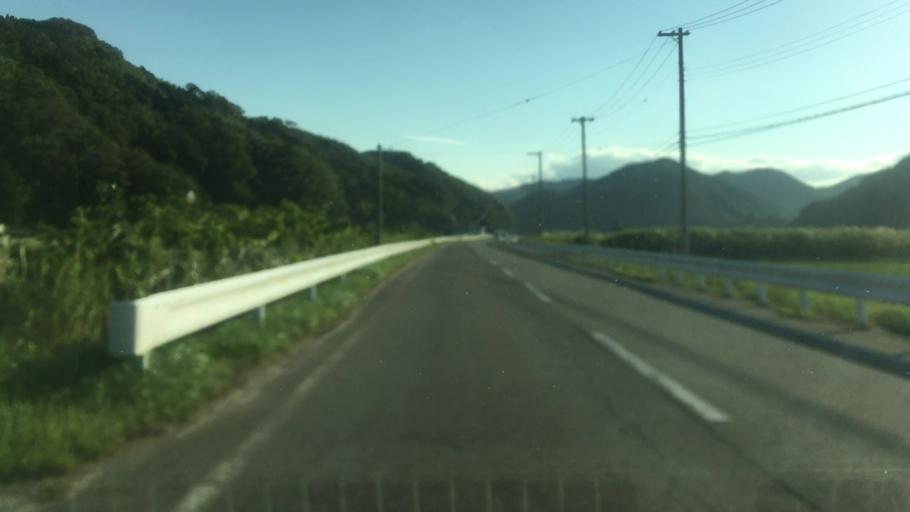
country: JP
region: Hyogo
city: Toyooka
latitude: 35.6173
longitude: 134.8141
